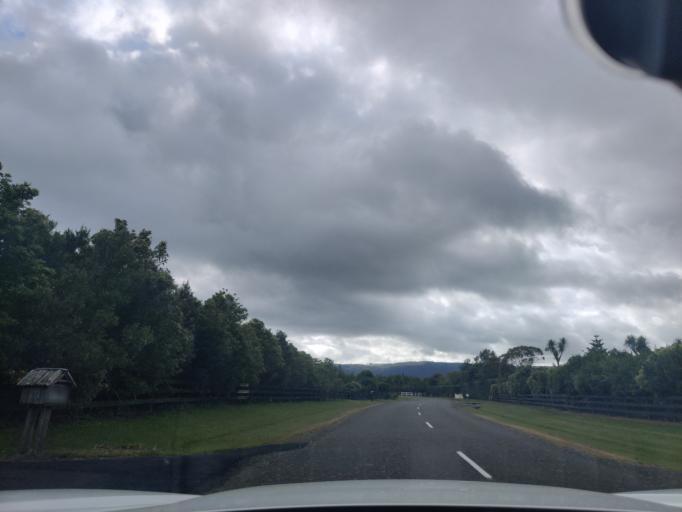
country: NZ
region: Manawatu-Wanganui
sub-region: Palmerston North City
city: Palmerston North
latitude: -40.3766
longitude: 175.6569
